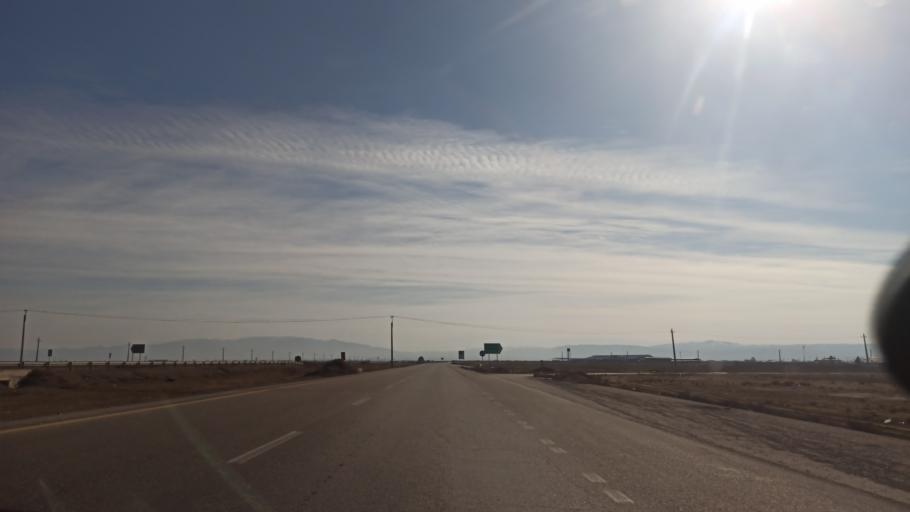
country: IR
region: Qazvin
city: Bu'in Zahra
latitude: 35.8185
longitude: 50.0756
